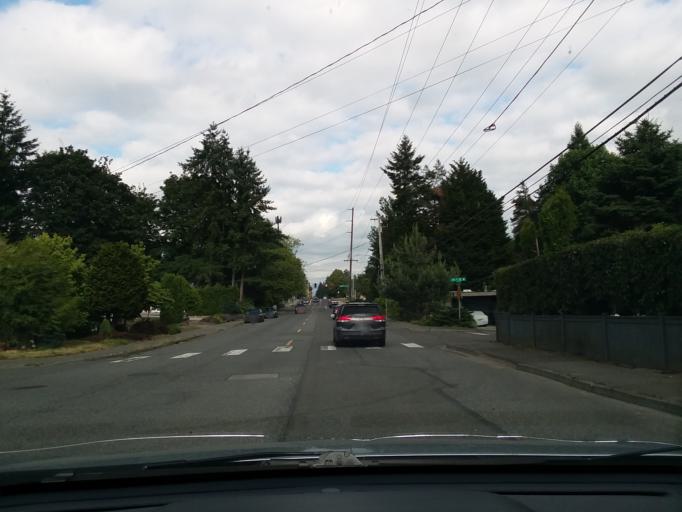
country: US
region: Washington
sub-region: Snohomish County
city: Mountlake Terrace
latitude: 47.7919
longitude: -122.2947
